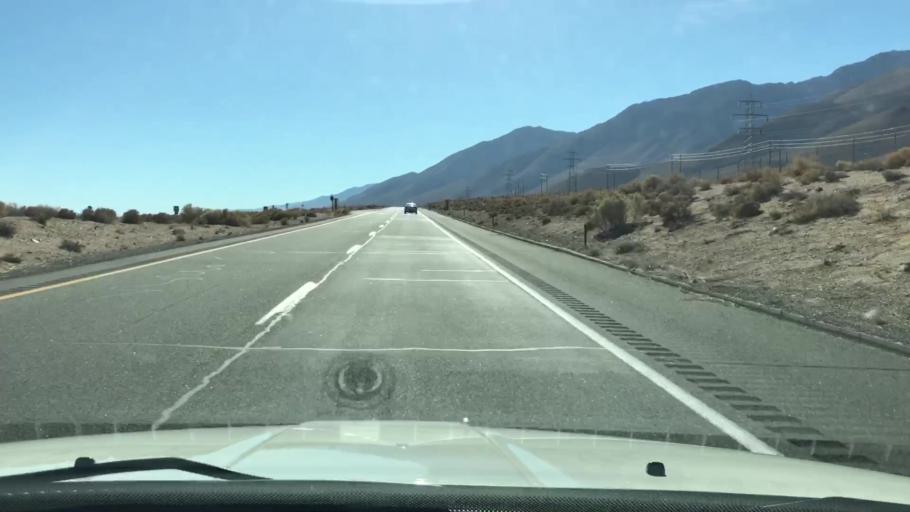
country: US
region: California
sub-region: Inyo County
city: Lone Pine
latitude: 36.4842
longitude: -118.0350
